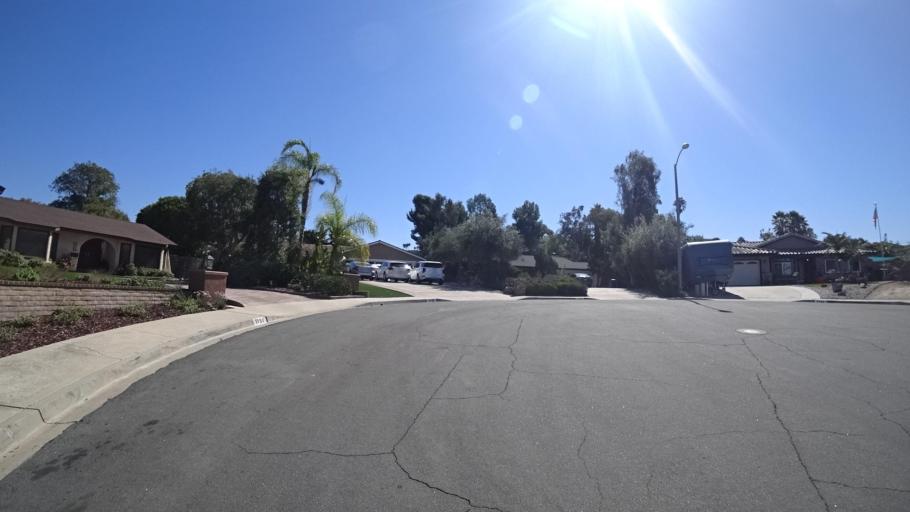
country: US
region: California
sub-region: San Diego County
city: Bonita
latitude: 32.6645
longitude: -117.0177
